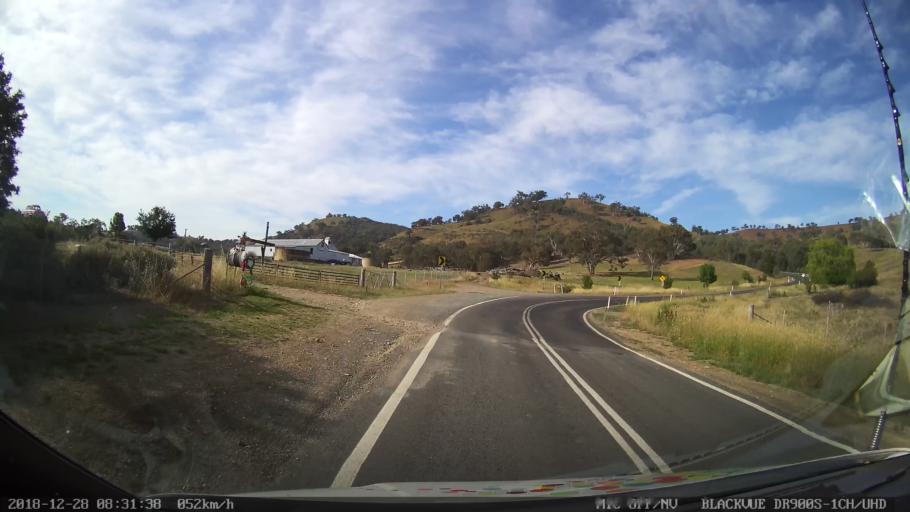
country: AU
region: New South Wales
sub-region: Blayney
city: Blayney
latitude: -33.9605
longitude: 149.3176
